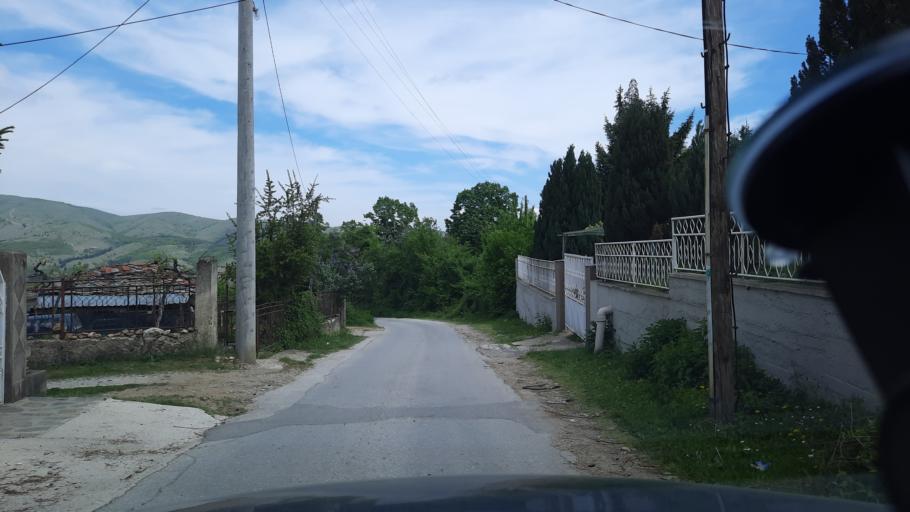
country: MK
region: Bitola
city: Bitola
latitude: 41.0254
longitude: 21.2855
